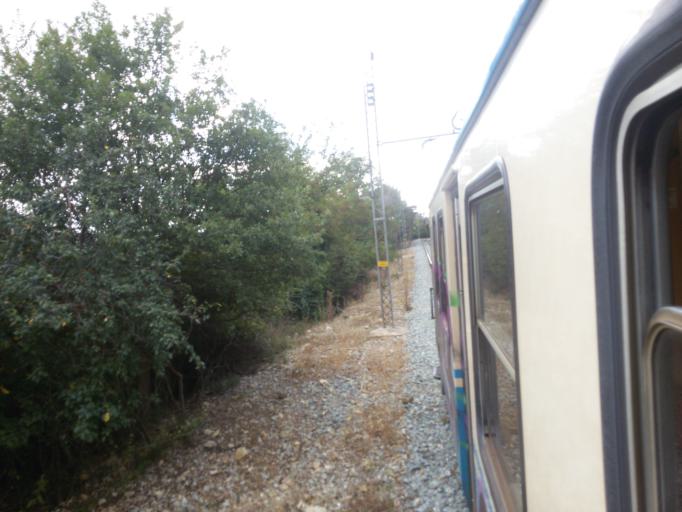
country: IT
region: Liguria
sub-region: Provincia di Genova
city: Genoa
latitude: 44.4434
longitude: 8.9431
